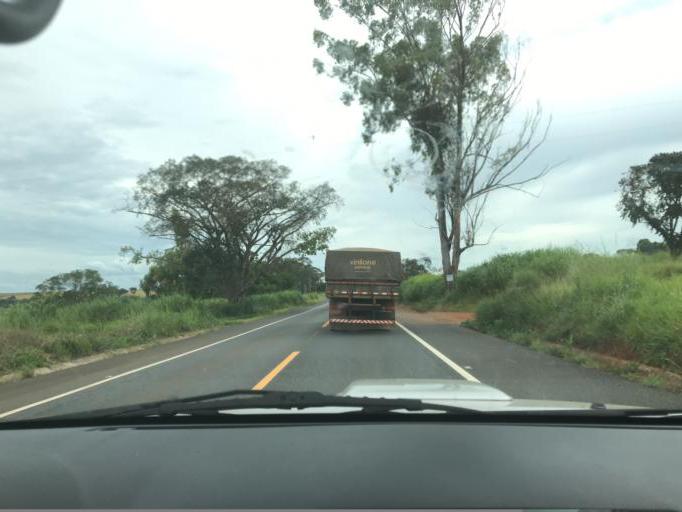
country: BR
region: Minas Gerais
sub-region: Araxa
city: Araxa
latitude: -19.3733
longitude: -46.8568
